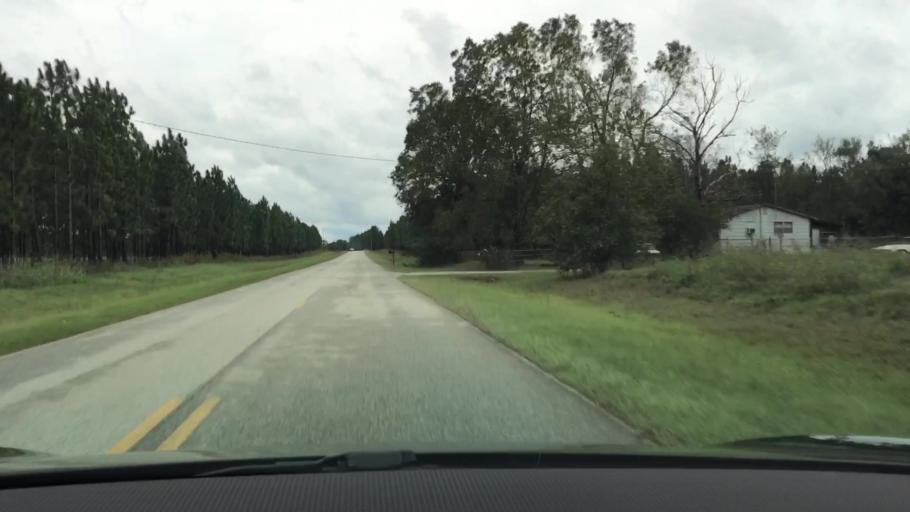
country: US
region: Georgia
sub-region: Jefferson County
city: Wadley
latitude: 32.8309
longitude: -82.3863
